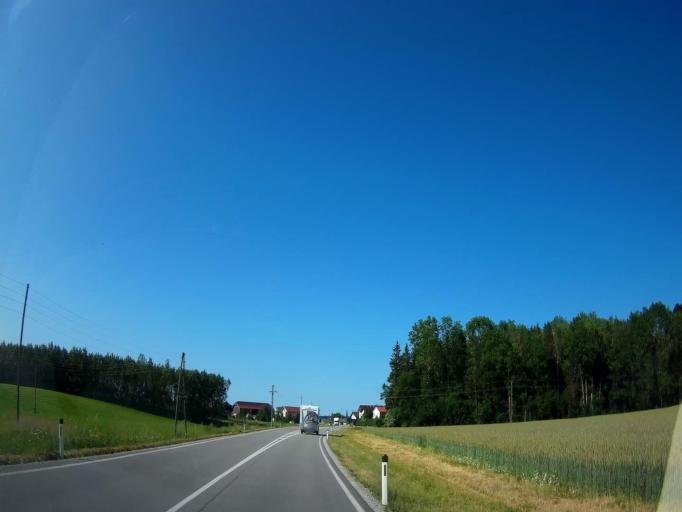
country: AT
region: Upper Austria
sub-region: Politischer Bezirk Braunau am Inn
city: Braunau am Inn
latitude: 48.1617
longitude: 13.0486
